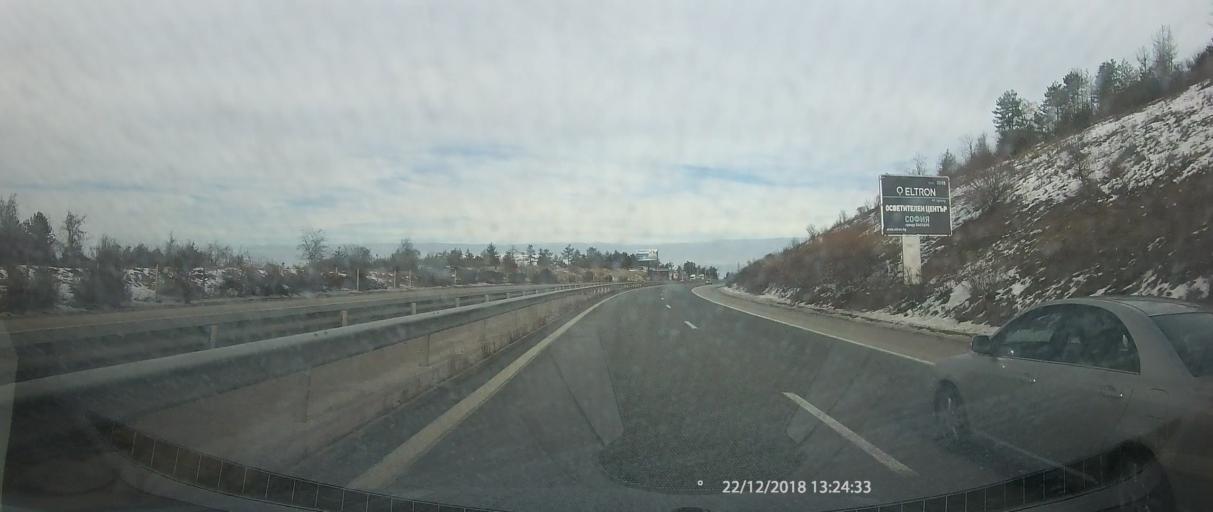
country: BG
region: Lovech
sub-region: Obshtina Yablanitsa
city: Yablanitsa
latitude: 43.0207
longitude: 24.1086
